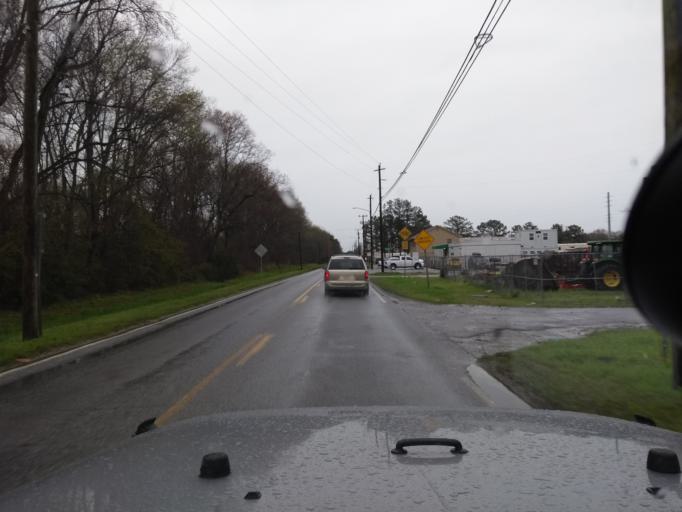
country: US
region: Georgia
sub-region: Chatham County
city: Garden City
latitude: 32.0862
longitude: -81.1394
